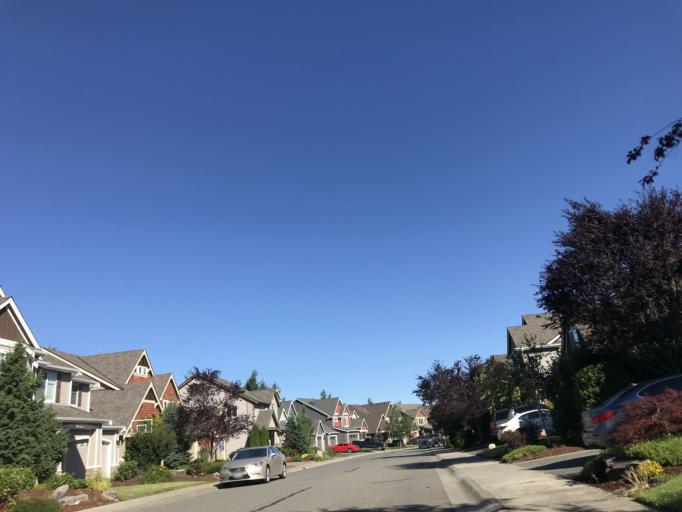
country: US
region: Washington
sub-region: King County
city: Ravensdale
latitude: 47.3535
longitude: -122.0035
